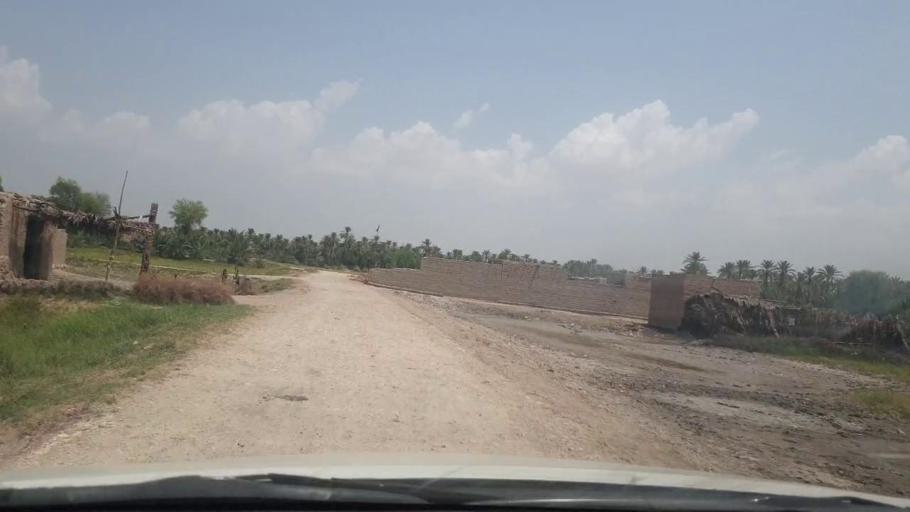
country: PK
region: Sindh
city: Khairpur
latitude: 27.5474
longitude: 68.8252
